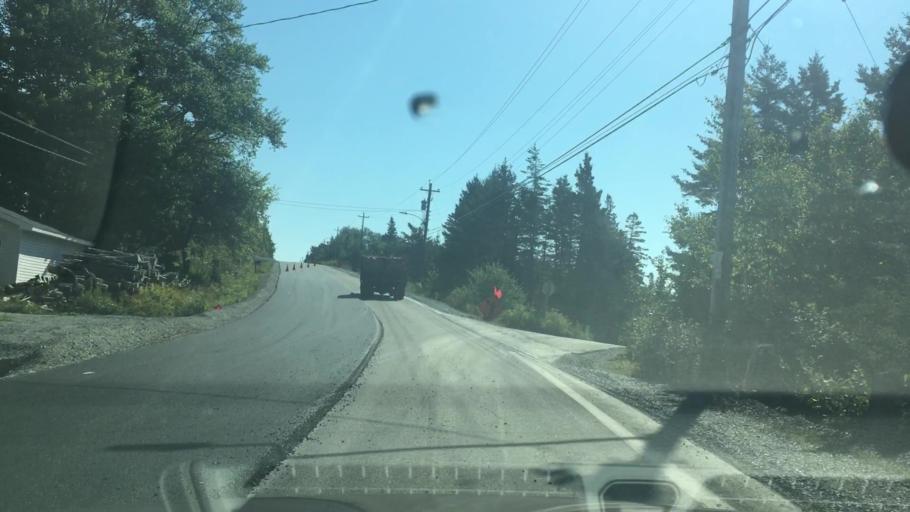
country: CA
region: Nova Scotia
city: New Glasgow
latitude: 44.9108
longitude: -62.5057
